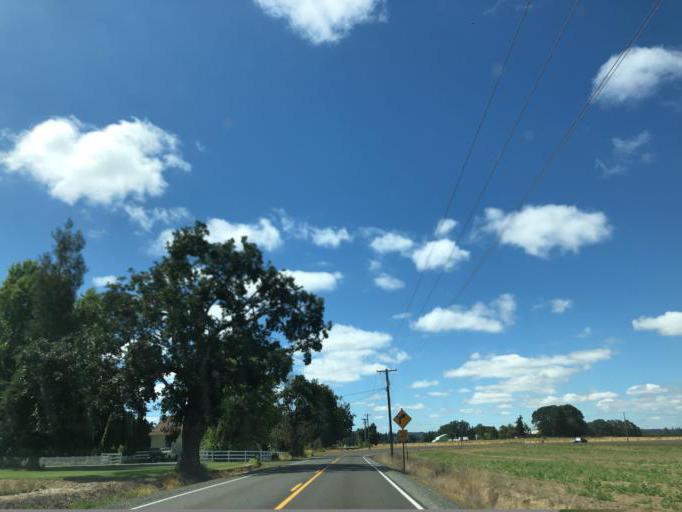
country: US
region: Oregon
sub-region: Marion County
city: Silverton
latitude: 45.0445
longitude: -122.7436
